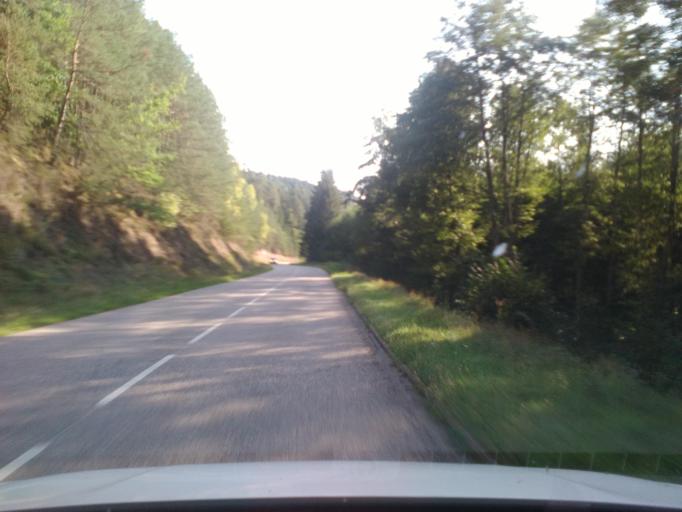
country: FR
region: Lorraine
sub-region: Departement des Vosges
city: Taintrux
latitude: 48.2254
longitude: 6.9045
